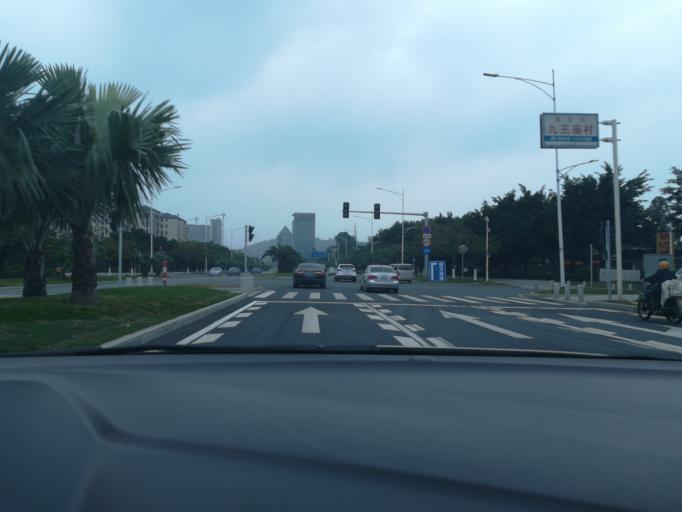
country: CN
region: Guangdong
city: Nansha
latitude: 22.7798
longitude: 113.5950
